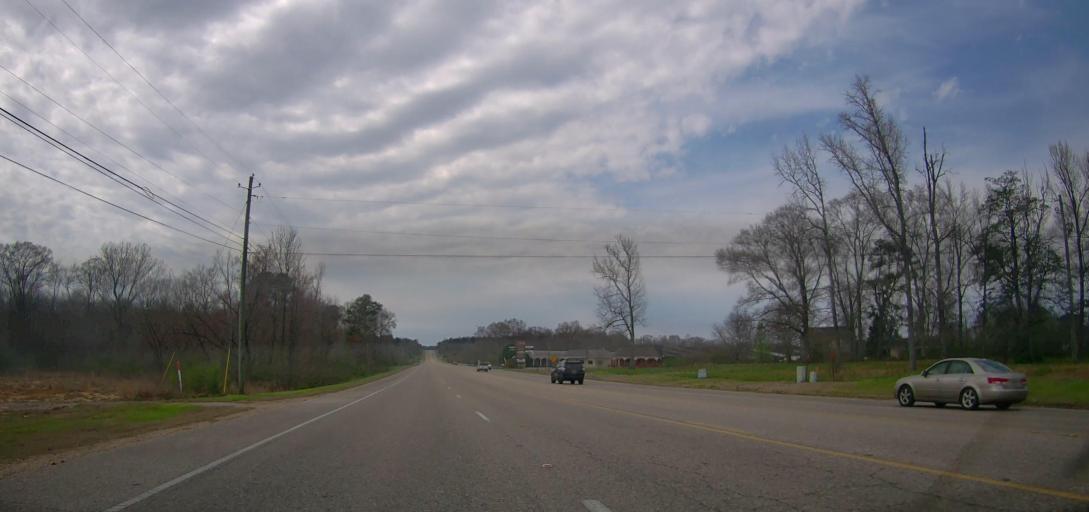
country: US
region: Alabama
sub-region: Marion County
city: Winfield
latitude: 33.9399
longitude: -87.8441
